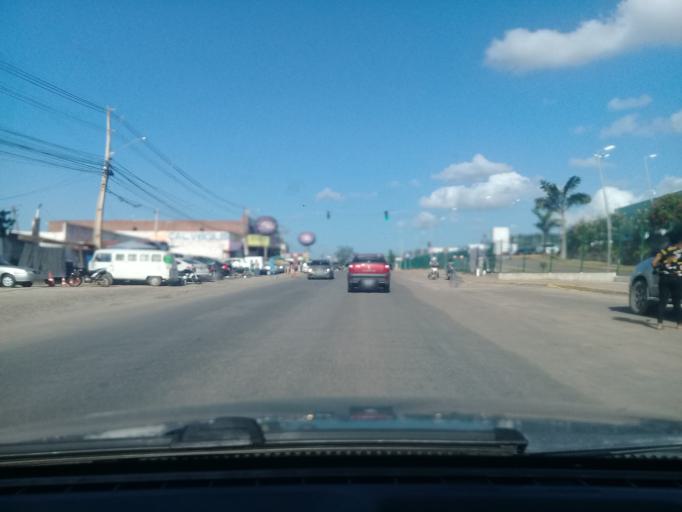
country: BR
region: Pernambuco
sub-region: Vitoria De Santo Antao
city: Vitoria de Santo Antao
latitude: -8.1154
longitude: -35.2719
